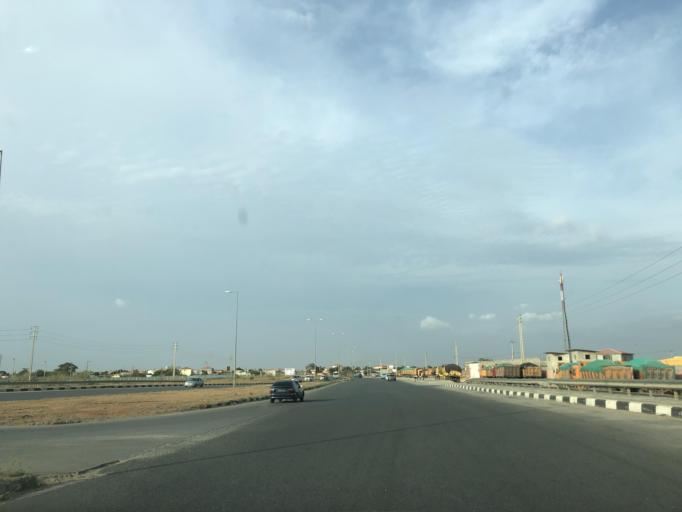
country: AO
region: Luanda
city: Luanda
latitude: -8.9341
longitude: 13.2997
